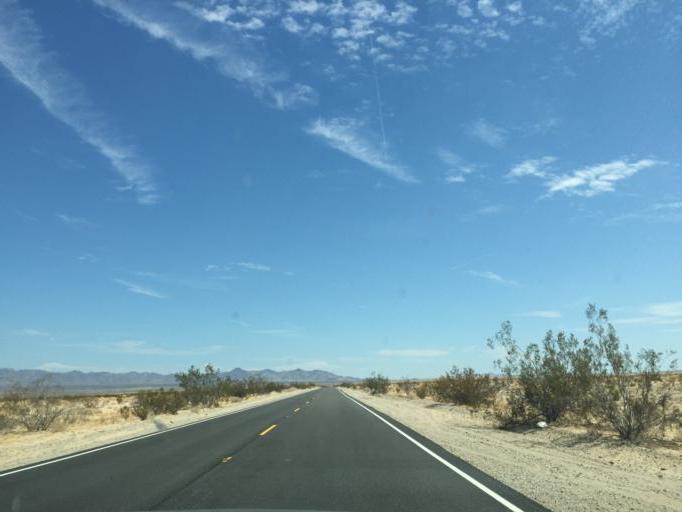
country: US
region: California
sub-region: Riverside County
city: Mesa Verde
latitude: 34.0970
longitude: -115.0282
